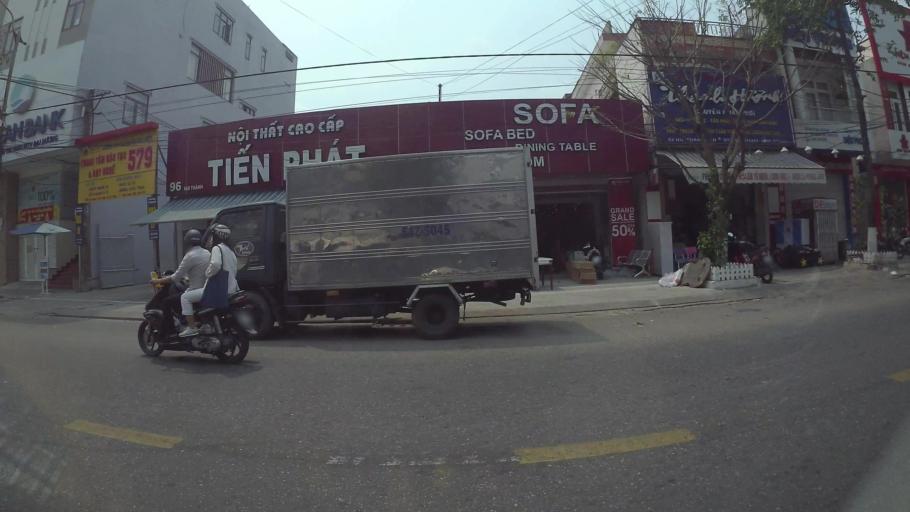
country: VN
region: Da Nang
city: Son Tra
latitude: 16.0514
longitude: 108.2205
